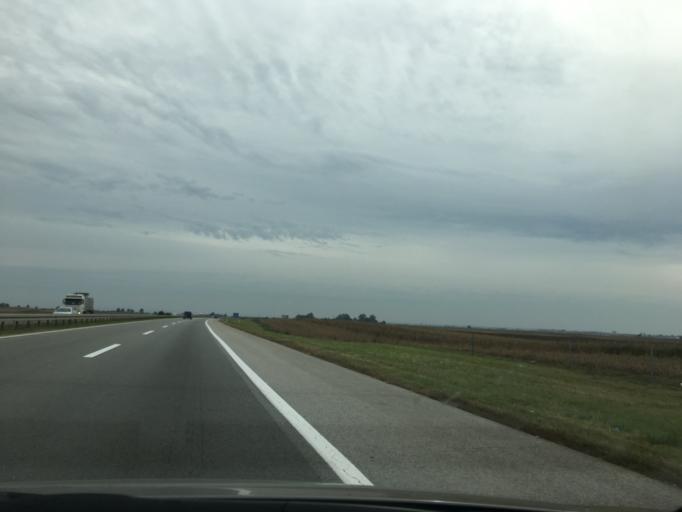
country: RS
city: Novi Banovci
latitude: 44.9289
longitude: 20.3000
